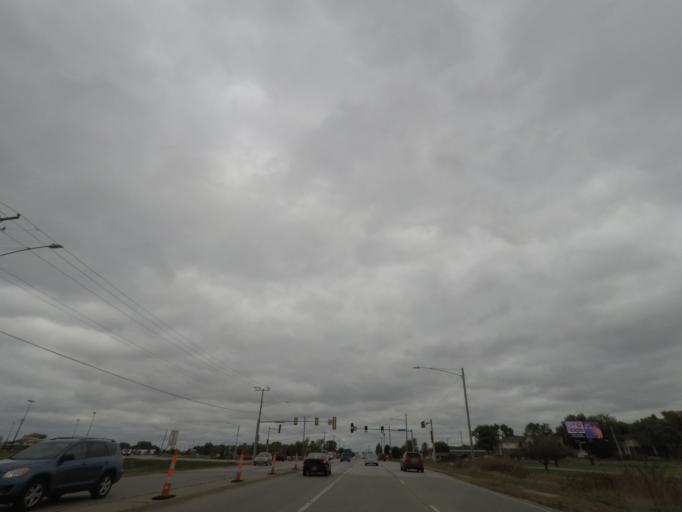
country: US
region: Iowa
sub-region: Polk County
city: Ankeny
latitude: 41.7190
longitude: -93.6004
